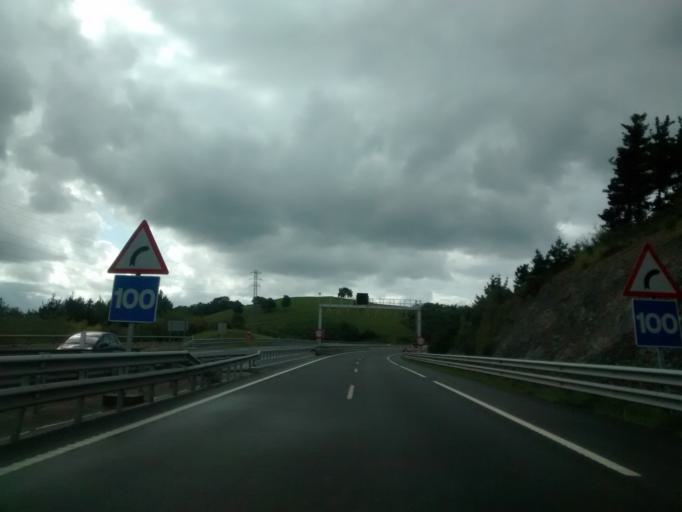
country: ES
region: Basque Country
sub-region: Provincia de Guipuzcoa
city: Lasarte
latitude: 43.2793
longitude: -2.0189
